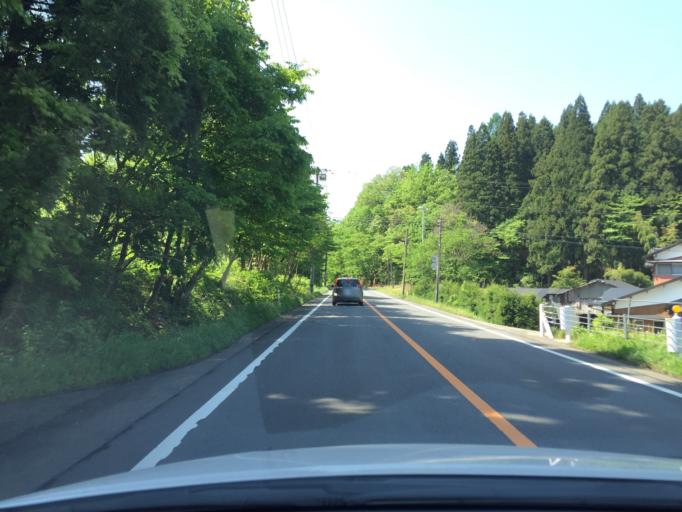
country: JP
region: Niigata
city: Muramatsu
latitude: 37.6569
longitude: 139.1373
